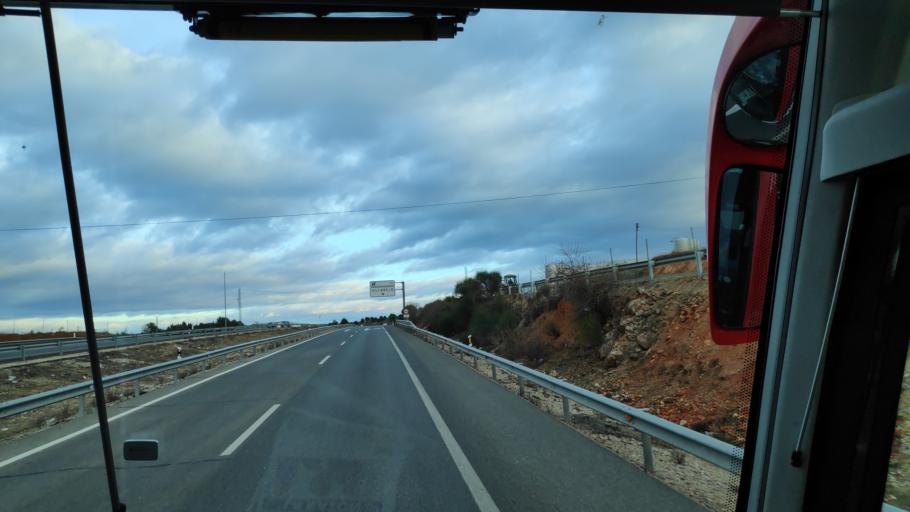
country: ES
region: Madrid
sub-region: Provincia de Madrid
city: Villarejo de Salvanes
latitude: 40.1638
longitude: -3.2746
